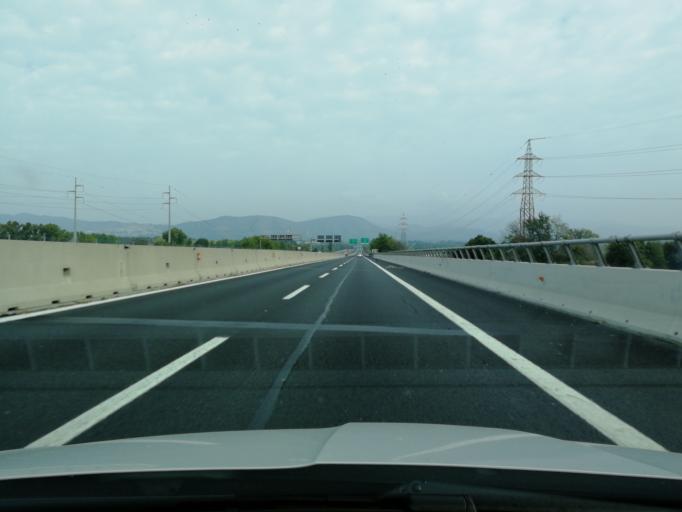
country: IT
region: Latium
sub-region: Citta metropolitana di Roma Capitale
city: Bagni di Tivoli
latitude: 41.9265
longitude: 12.7163
